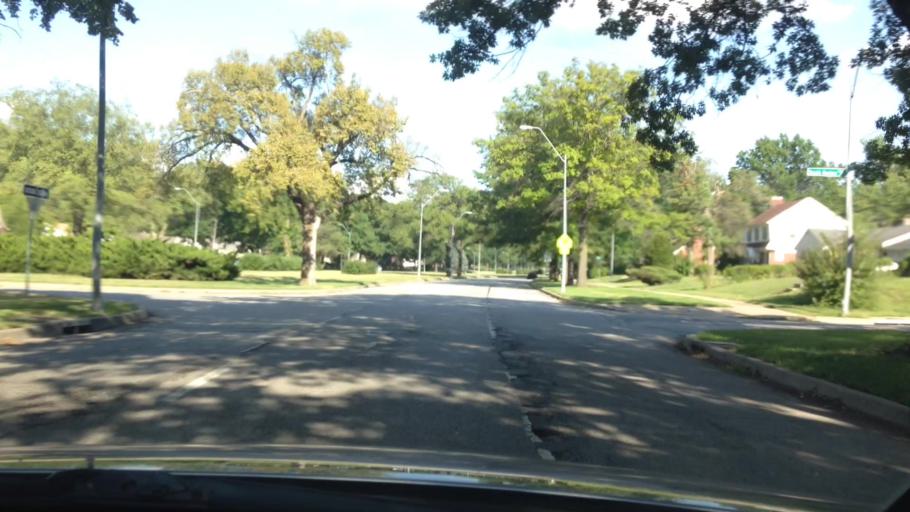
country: US
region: Kansas
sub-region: Johnson County
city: Mission Hills
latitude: 39.0075
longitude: -94.5532
